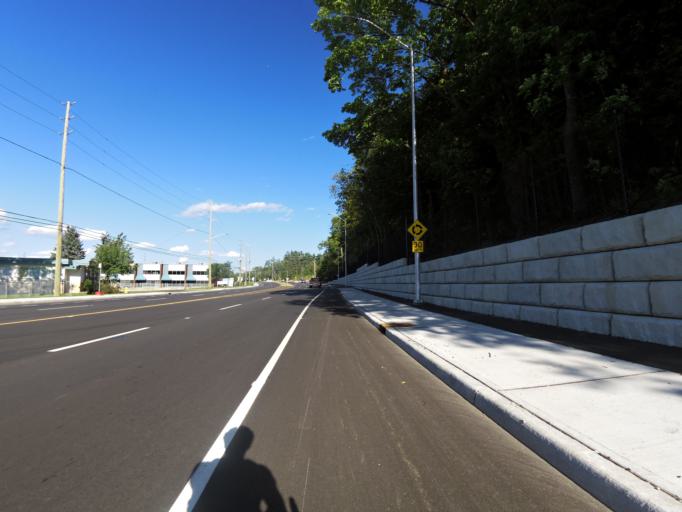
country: CA
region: Ontario
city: Clarence-Rockland
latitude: 45.4885
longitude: -75.4808
